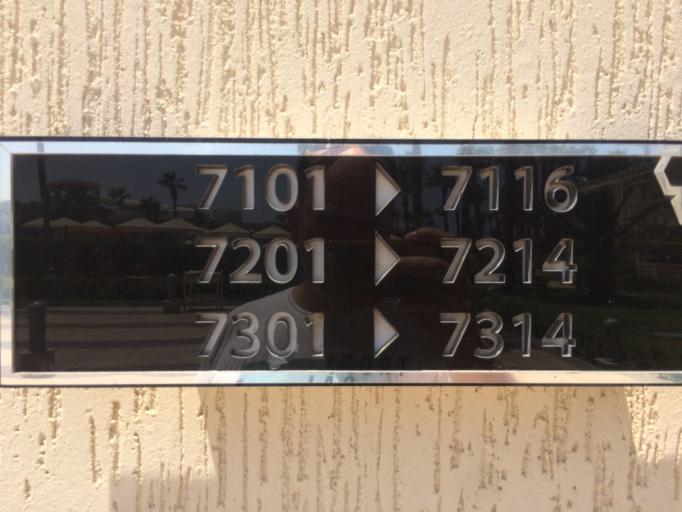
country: EG
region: Red Sea
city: Hurghada
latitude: 27.1228
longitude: 33.8250
